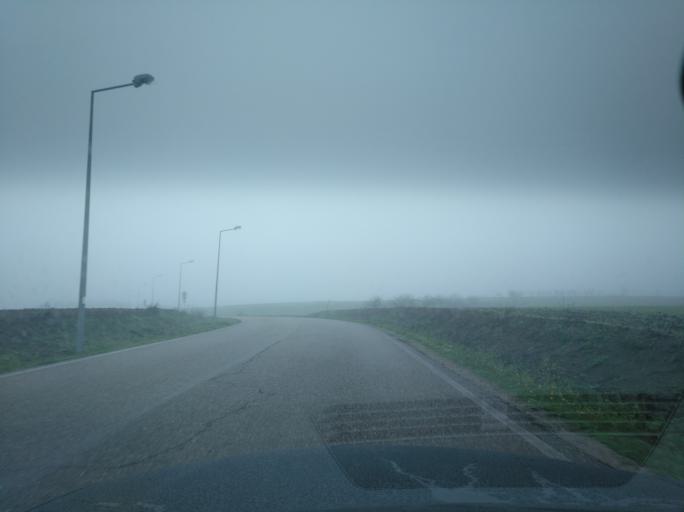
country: PT
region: Portalegre
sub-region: Campo Maior
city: Campo Maior
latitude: 39.0262
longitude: -7.0687
